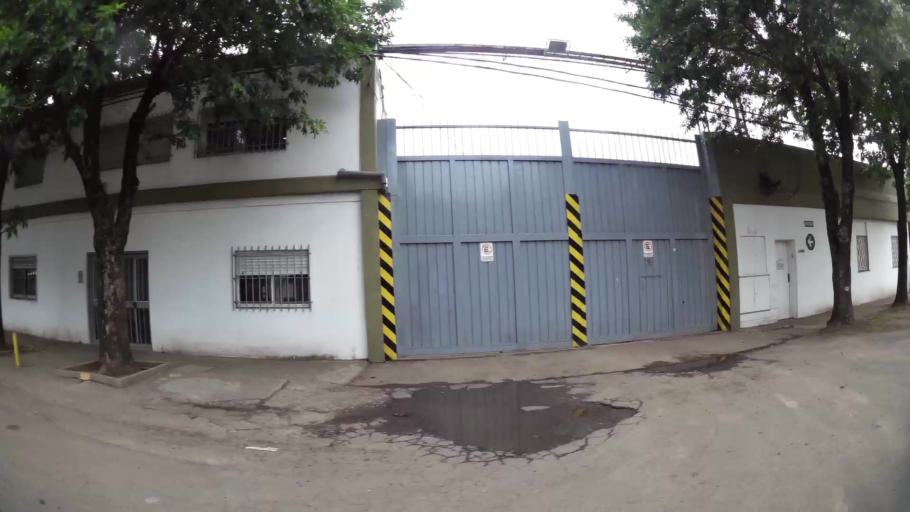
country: AR
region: Santa Fe
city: Gobernador Galvez
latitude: -33.0063
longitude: -60.6581
